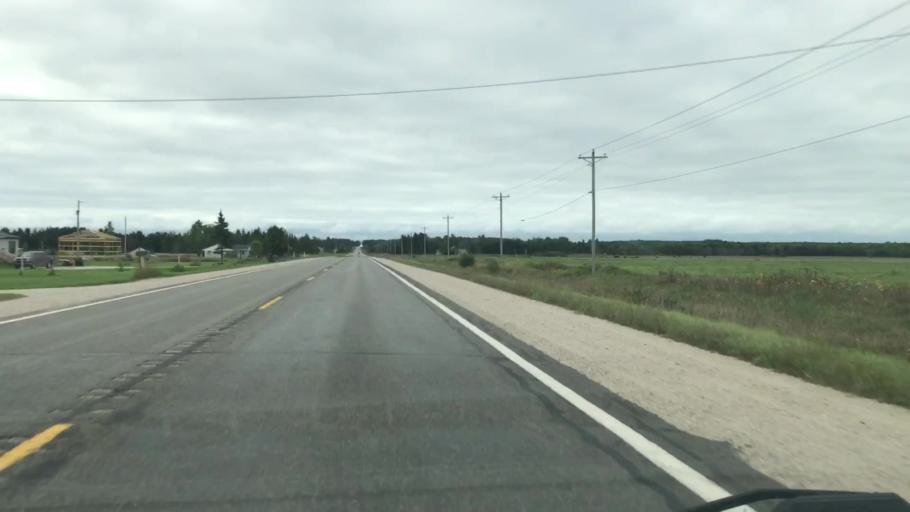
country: US
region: Michigan
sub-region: Luce County
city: Newberry
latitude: 46.1471
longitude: -85.5713
